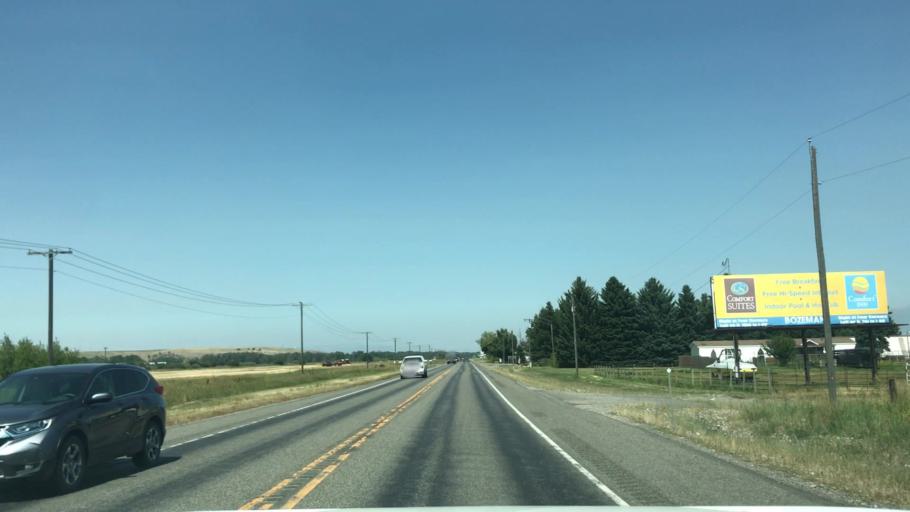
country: US
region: Montana
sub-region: Gallatin County
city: Four Corners
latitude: 45.6249
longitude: -111.1969
